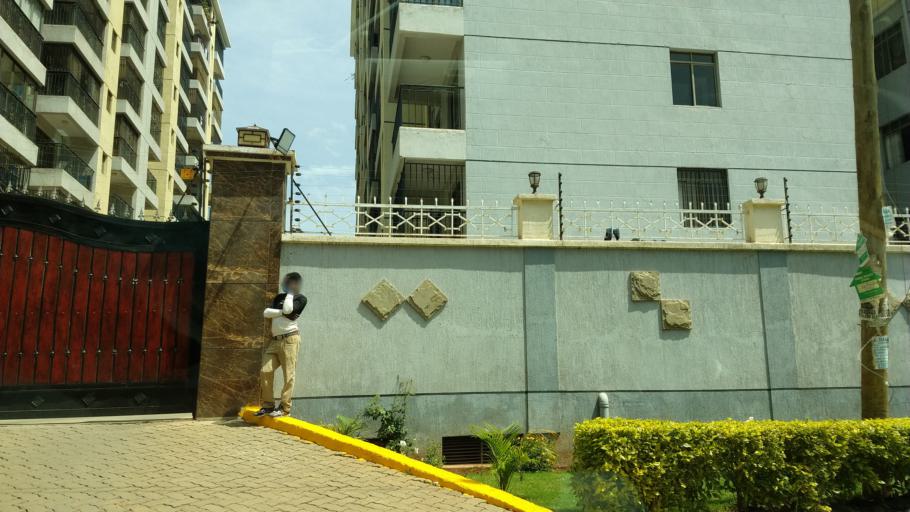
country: KE
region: Nairobi Area
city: Nairobi
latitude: -1.2976
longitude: 36.7866
